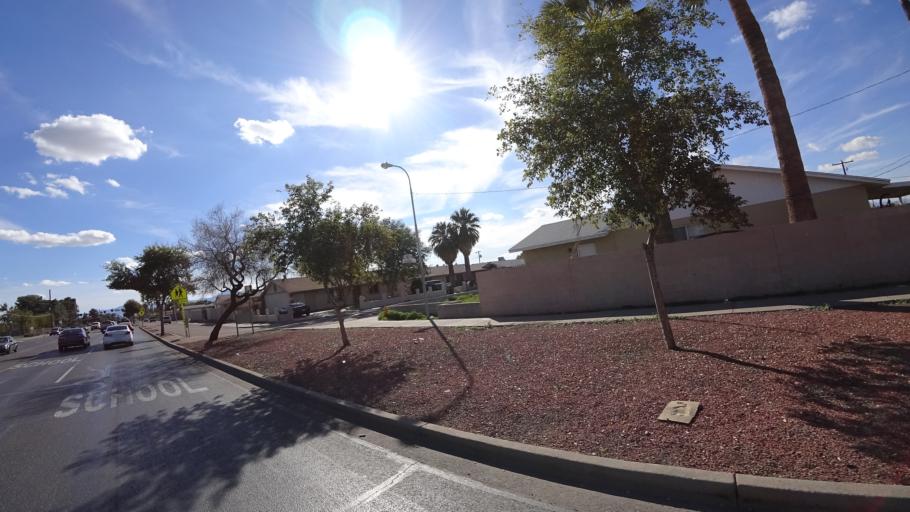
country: US
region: Arizona
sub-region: Maricopa County
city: Glendale
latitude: 33.4931
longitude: -112.2206
